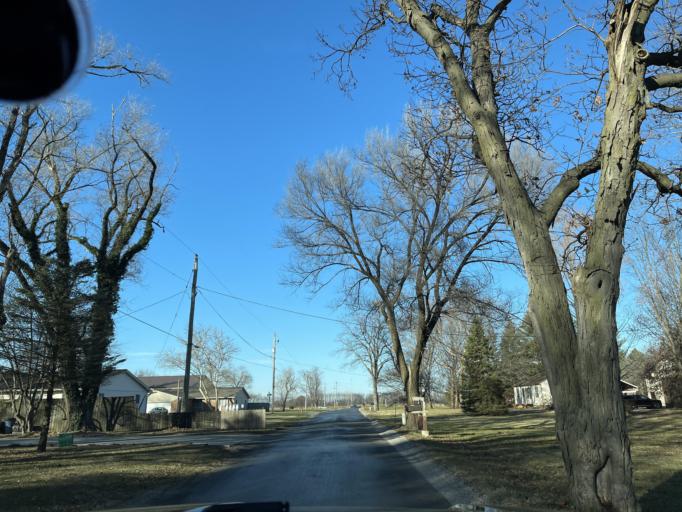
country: US
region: Illinois
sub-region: Sangamon County
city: Leland Grove
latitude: 39.8165
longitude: -89.7134
